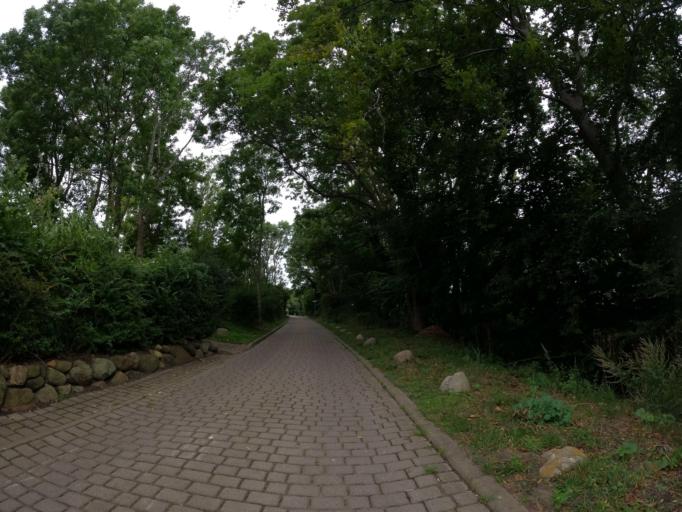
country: DE
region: Mecklenburg-Vorpommern
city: Ostseebad Sellin
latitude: 54.3049
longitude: 13.6655
